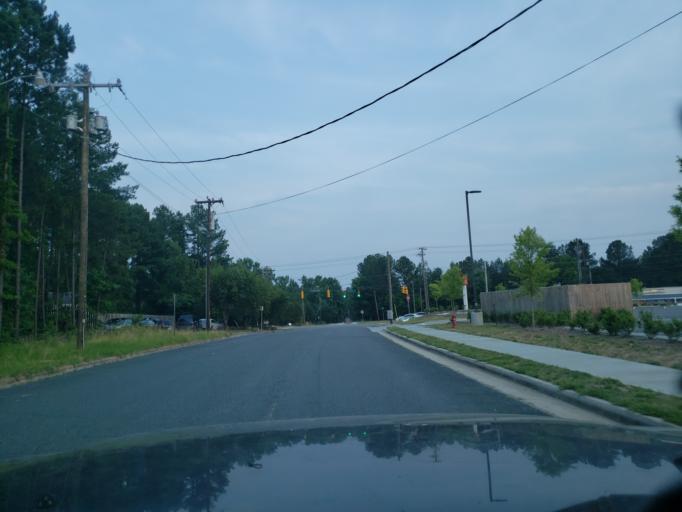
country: US
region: North Carolina
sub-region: Durham County
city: Gorman
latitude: 35.9876
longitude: -78.8440
